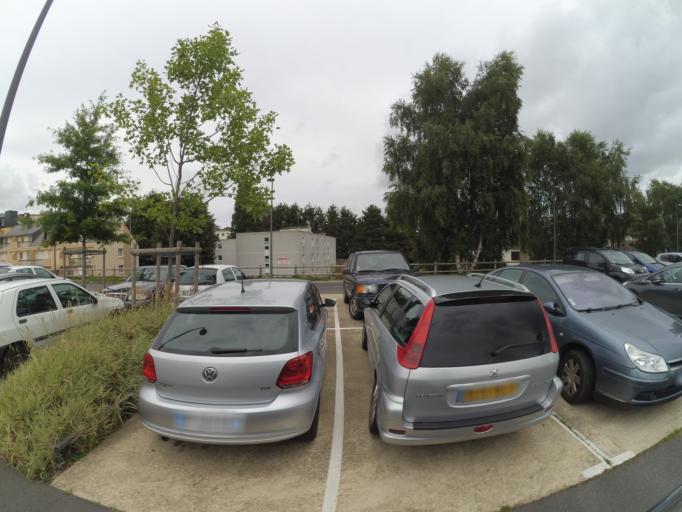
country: FR
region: Brittany
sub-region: Departement des Cotes-d'Armor
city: Guingamp
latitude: 48.5561
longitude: -3.1422
